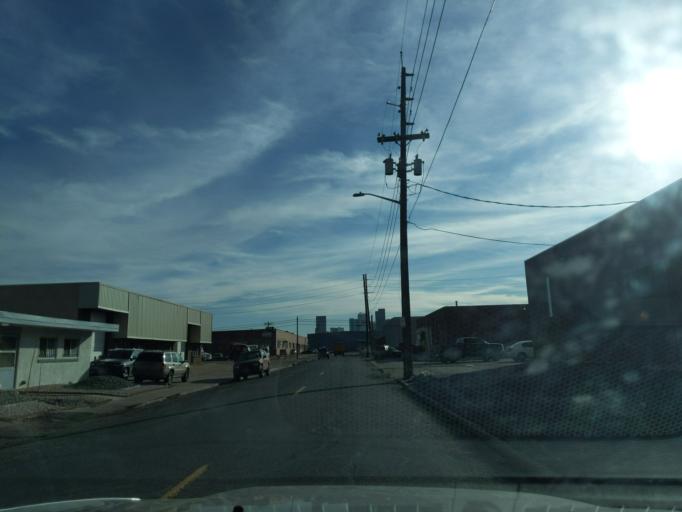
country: US
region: Colorado
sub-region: Denver County
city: Denver
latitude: 39.7762
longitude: -104.9876
